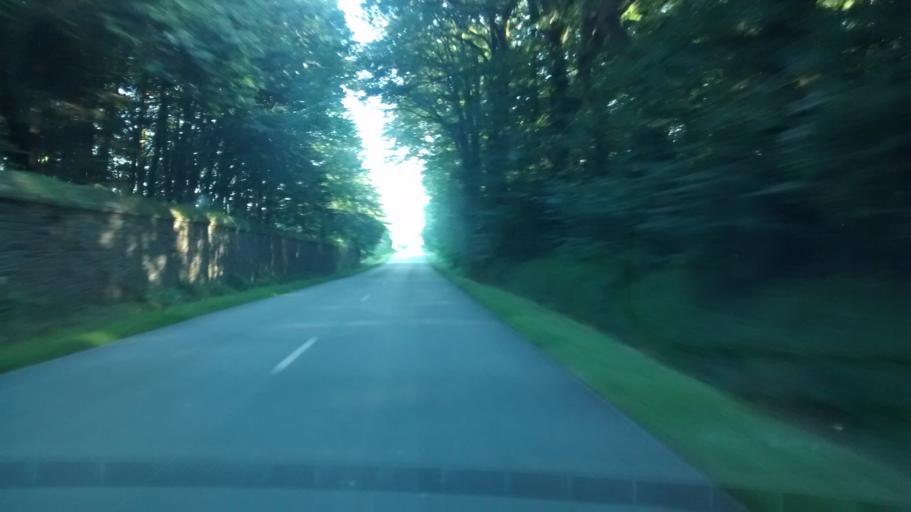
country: FR
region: Brittany
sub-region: Departement du Morbihan
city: Molac
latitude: 47.7611
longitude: -2.4363
